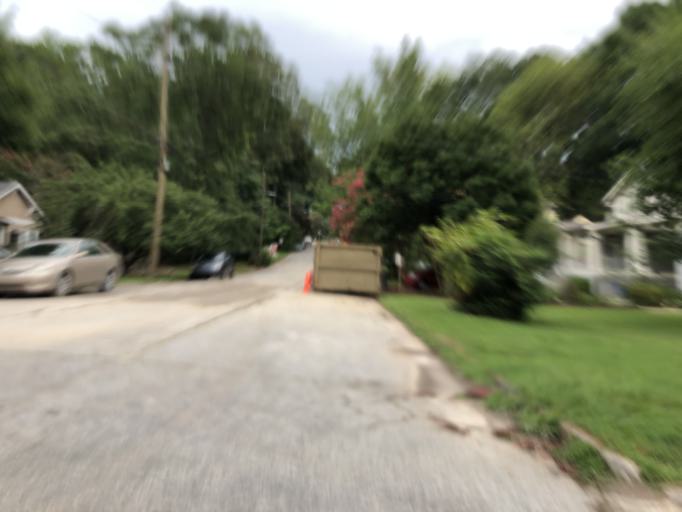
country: US
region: Georgia
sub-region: DeKalb County
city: Decatur
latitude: 33.7784
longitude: -84.3053
